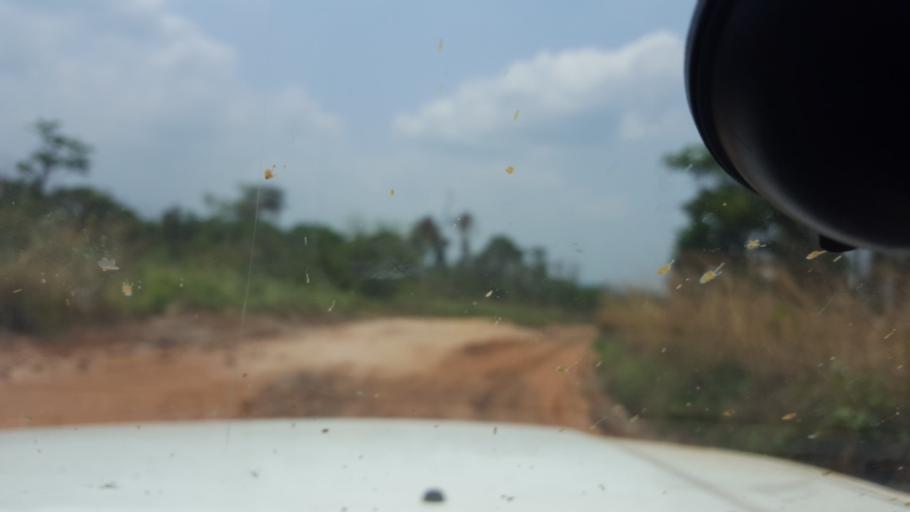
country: CD
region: Bandundu
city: Mushie
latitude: -3.7504
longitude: 16.6357
